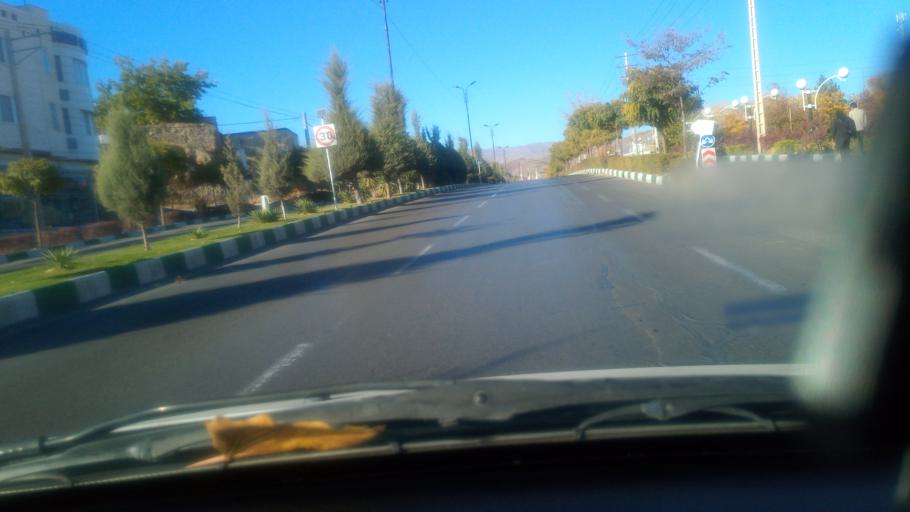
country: IR
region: Razavi Khorasan
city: Torqabeh
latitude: 36.3139
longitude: 59.3708
